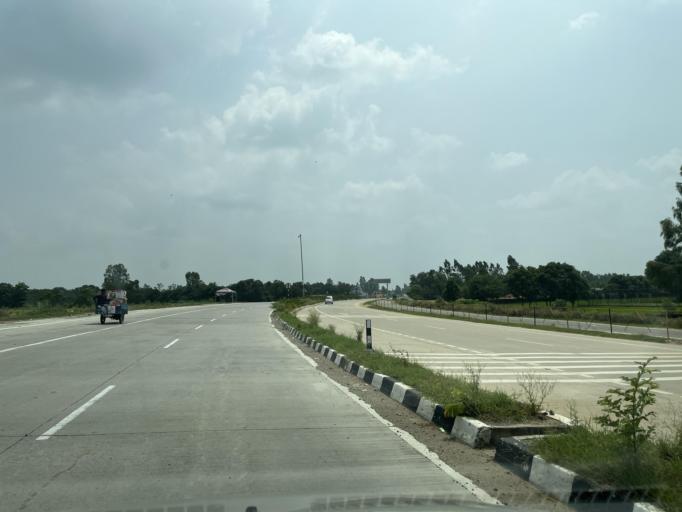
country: IN
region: Uttar Pradesh
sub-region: Bijnor
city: Nagina
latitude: 29.4236
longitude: 78.4441
